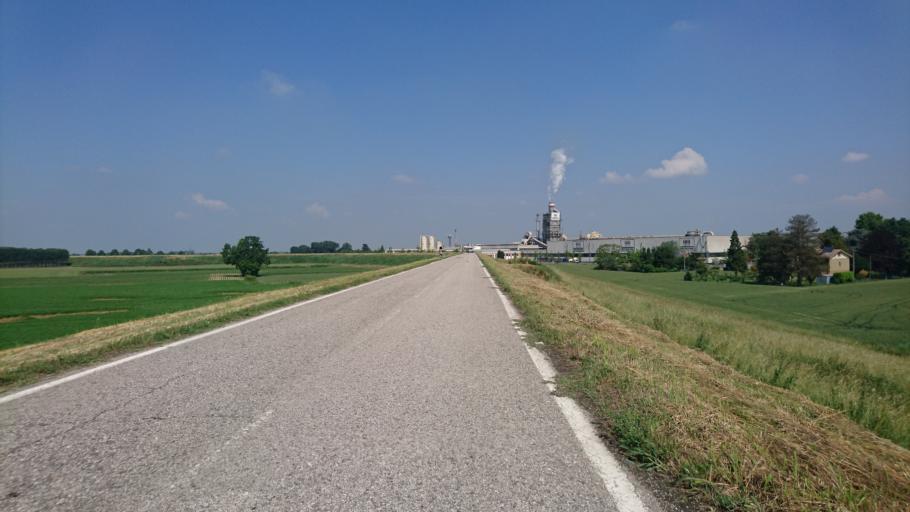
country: IT
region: Lombardy
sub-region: Provincia di Mantova
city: Sustinente
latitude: 45.0654
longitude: 11.0480
